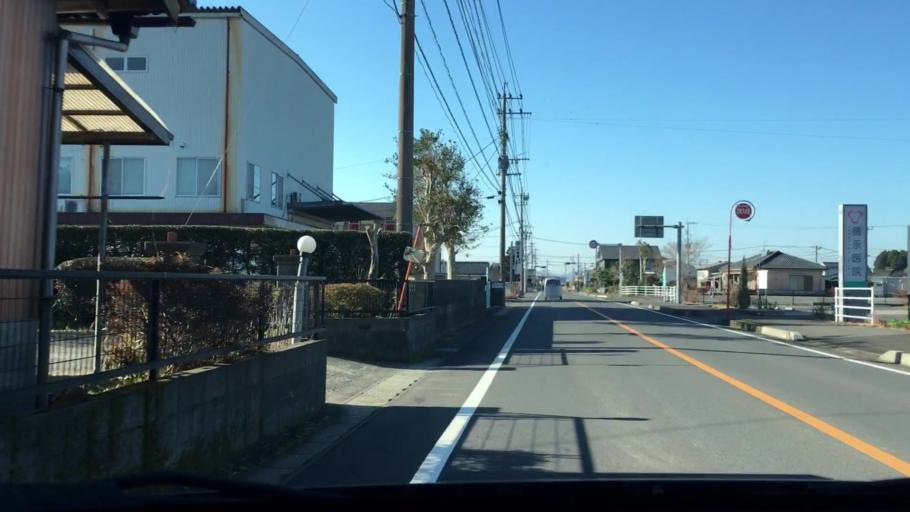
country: JP
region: Kagoshima
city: Kajiki
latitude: 31.7928
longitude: 130.7161
